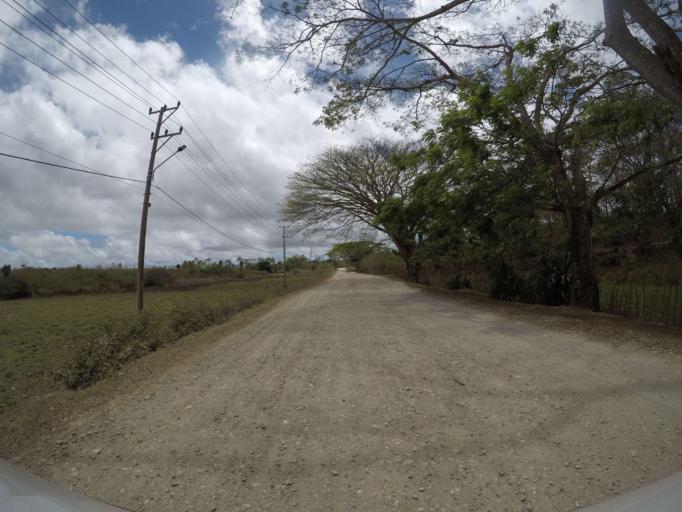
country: TL
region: Lautem
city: Lospalos
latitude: -8.4537
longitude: 127.0022
